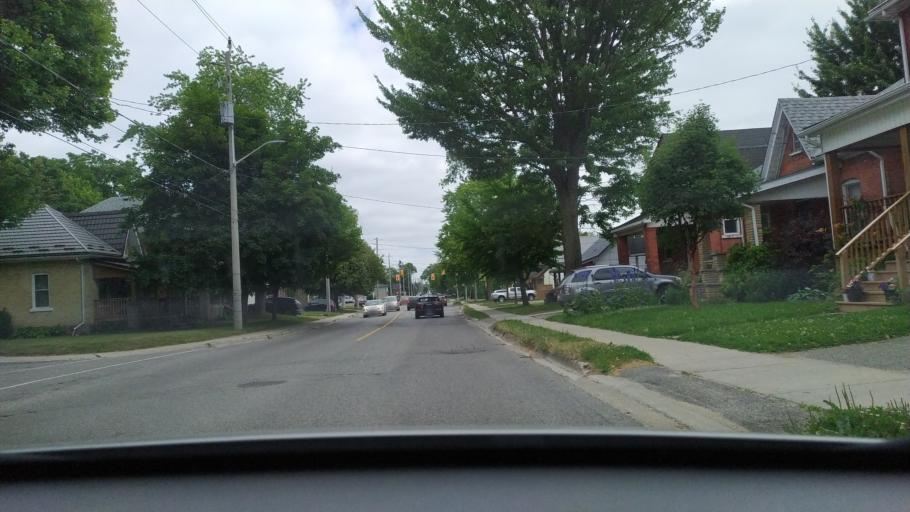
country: CA
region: Ontario
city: Stratford
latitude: 43.3614
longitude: -80.9771
